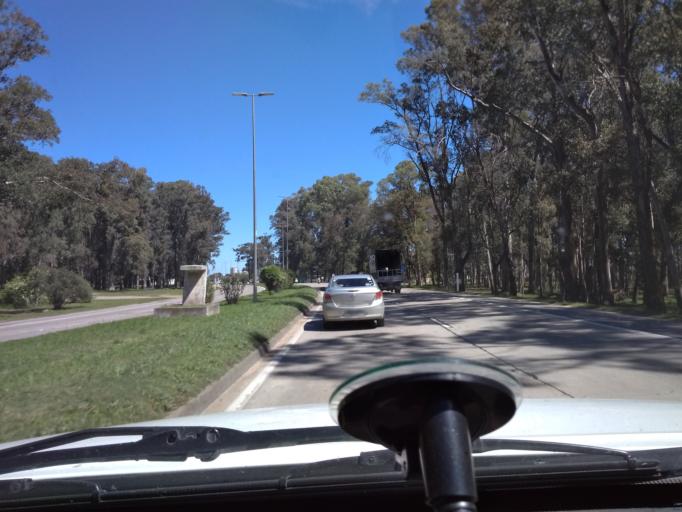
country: UY
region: Canelones
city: Barra de Carrasco
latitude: -34.8569
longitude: -56.0293
